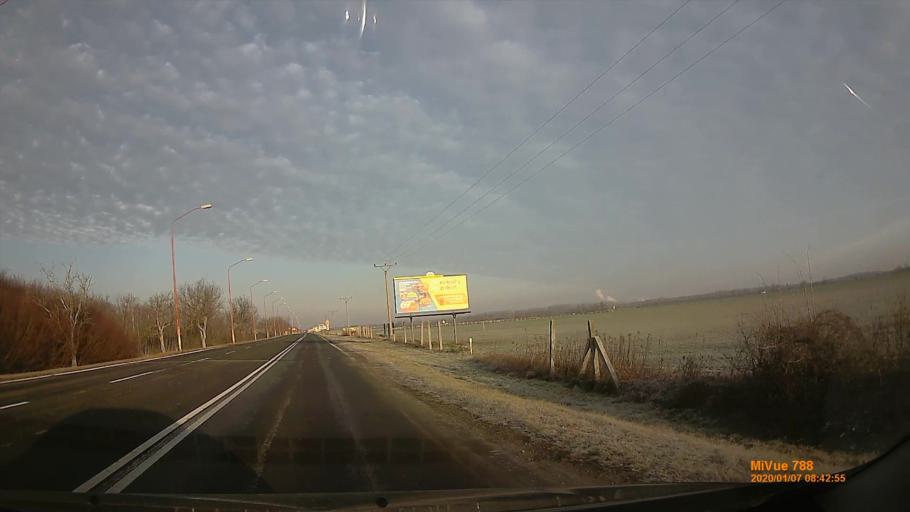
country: HU
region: Gyor-Moson-Sopron
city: Rajka
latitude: 48.0192
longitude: 17.1760
